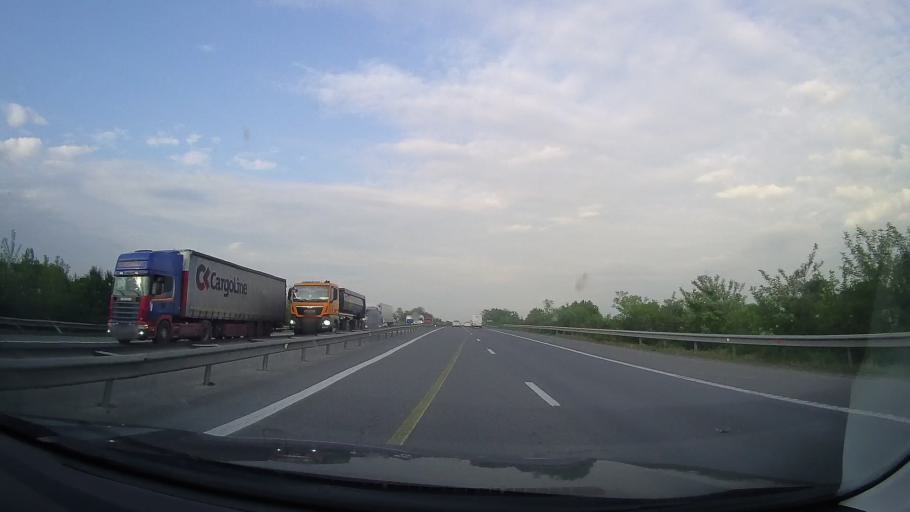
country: RO
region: Giurgiu
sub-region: Comuna Bolintin Vale
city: Bolintin Vale
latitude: 44.4679
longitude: 25.7681
